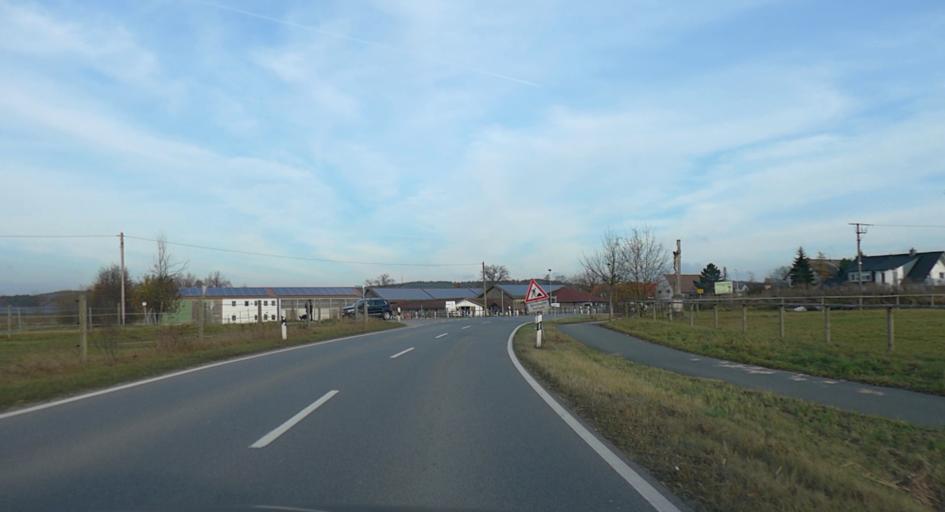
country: DE
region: Bavaria
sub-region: Upper Franconia
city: Poxdorf
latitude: 49.6638
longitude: 11.0632
